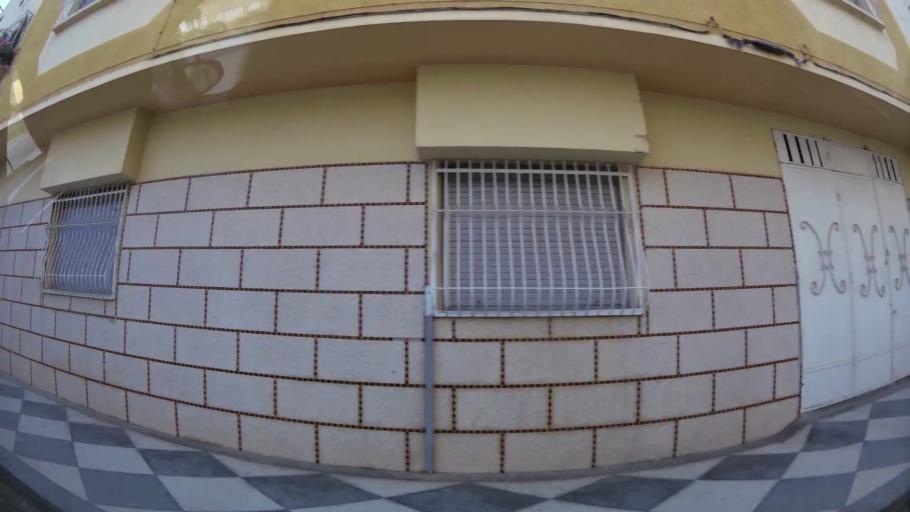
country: MA
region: Oriental
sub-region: Oujda-Angad
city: Oujda
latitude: 34.6934
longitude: -1.9012
